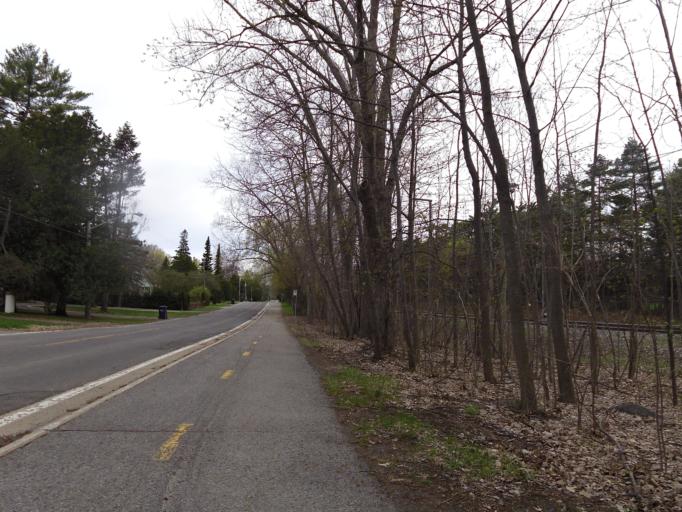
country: CA
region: Quebec
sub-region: Laurentides
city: Deux-Montagnes
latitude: 45.5248
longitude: -73.8743
